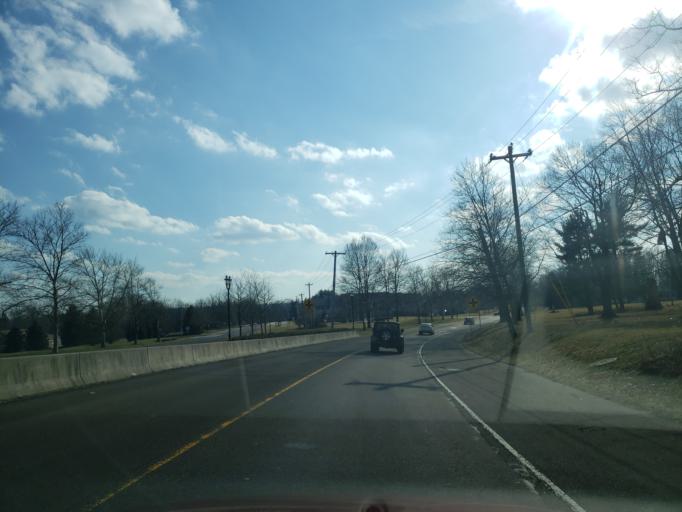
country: US
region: Pennsylvania
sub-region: Bucks County
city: Doylestown
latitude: 40.2928
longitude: -75.1279
